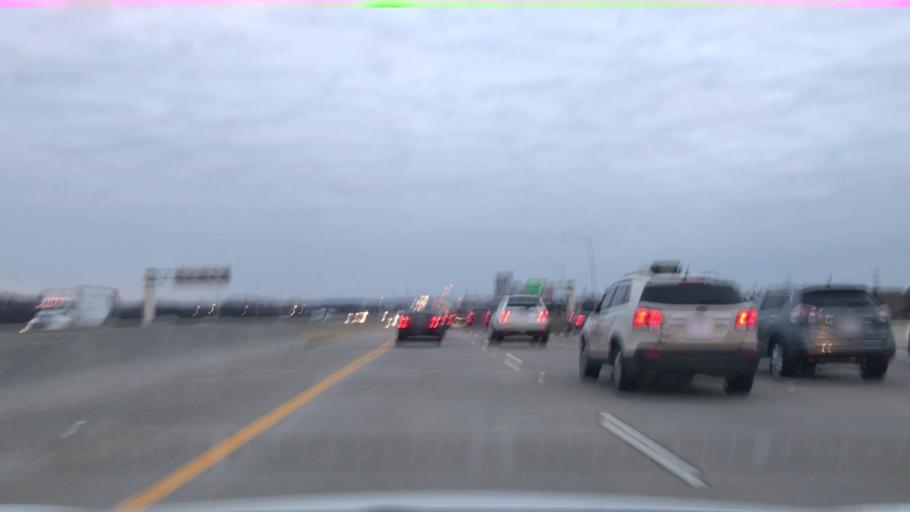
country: US
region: Texas
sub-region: Collin County
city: Plano
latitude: 33.0038
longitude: -96.7317
